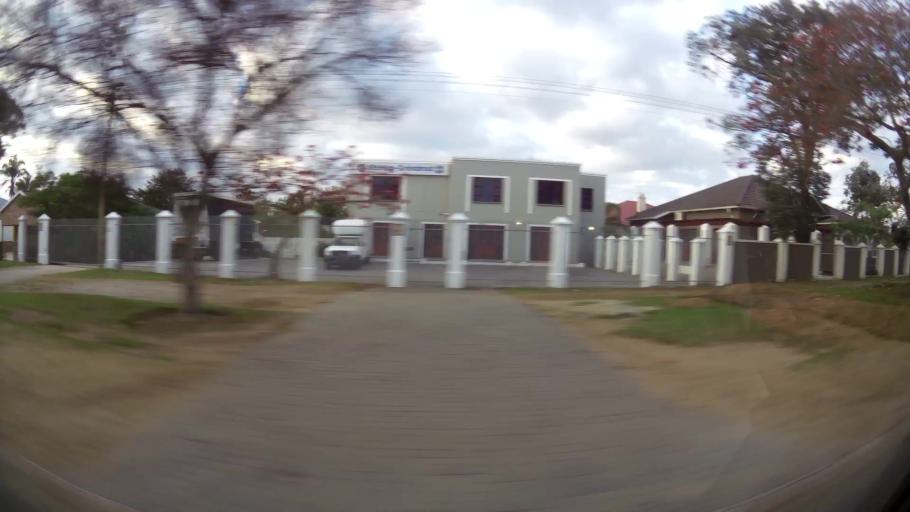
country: ZA
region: Eastern Cape
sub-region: Nelson Mandela Bay Metropolitan Municipality
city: Port Elizabeth
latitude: -33.9795
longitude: 25.6000
